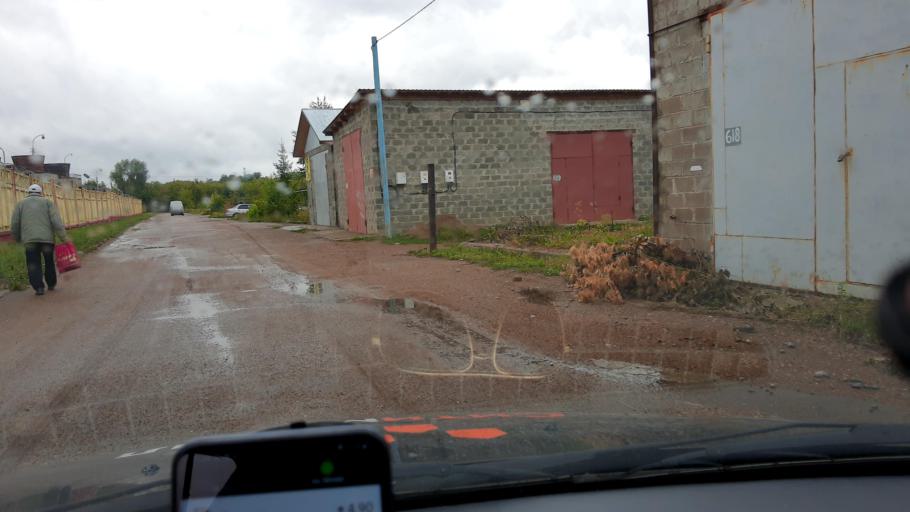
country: RU
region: Bashkortostan
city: Ufa
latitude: 54.7957
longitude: 56.0997
